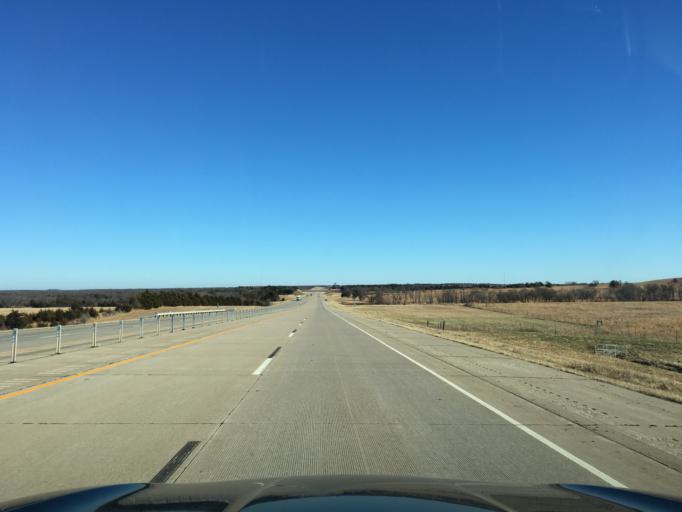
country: US
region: Oklahoma
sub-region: Payne County
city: Yale
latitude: 36.2251
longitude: -96.6359
